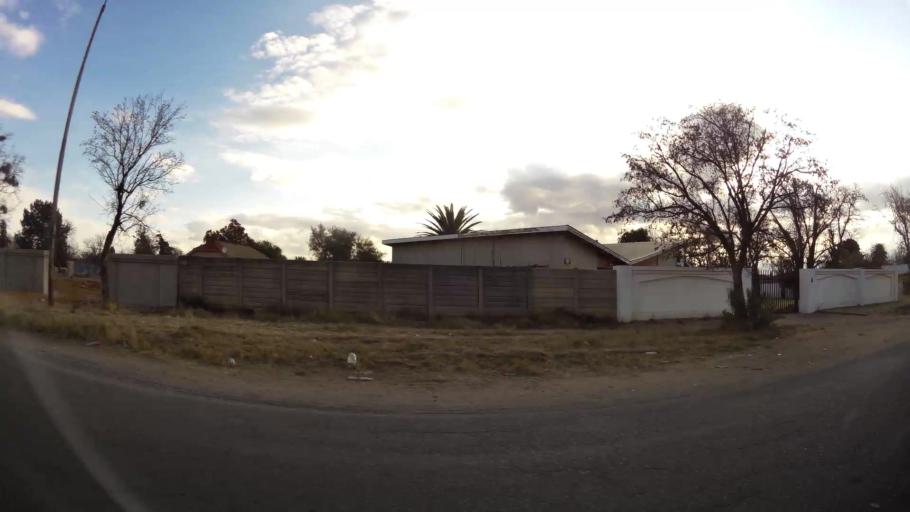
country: ZA
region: Orange Free State
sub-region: Lejweleputswa District Municipality
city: Welkom
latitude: -27.9843
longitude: 26.7118
